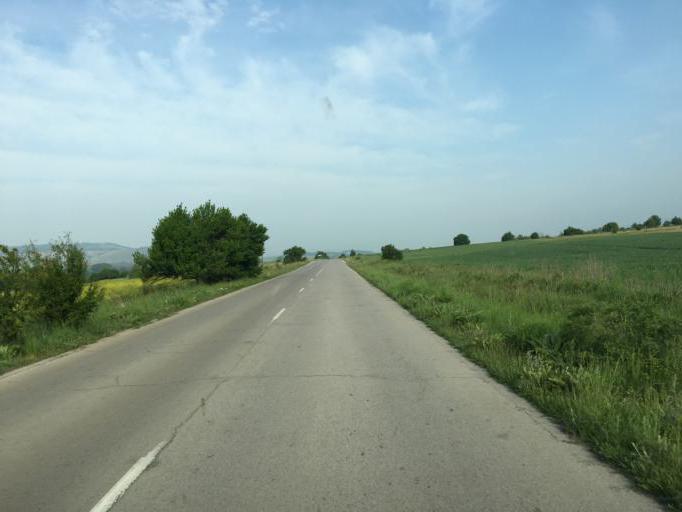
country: BG
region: Kyustendil
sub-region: Obshtina Bobovdol
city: Bobovdol
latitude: 42.4650
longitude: 23.0830
